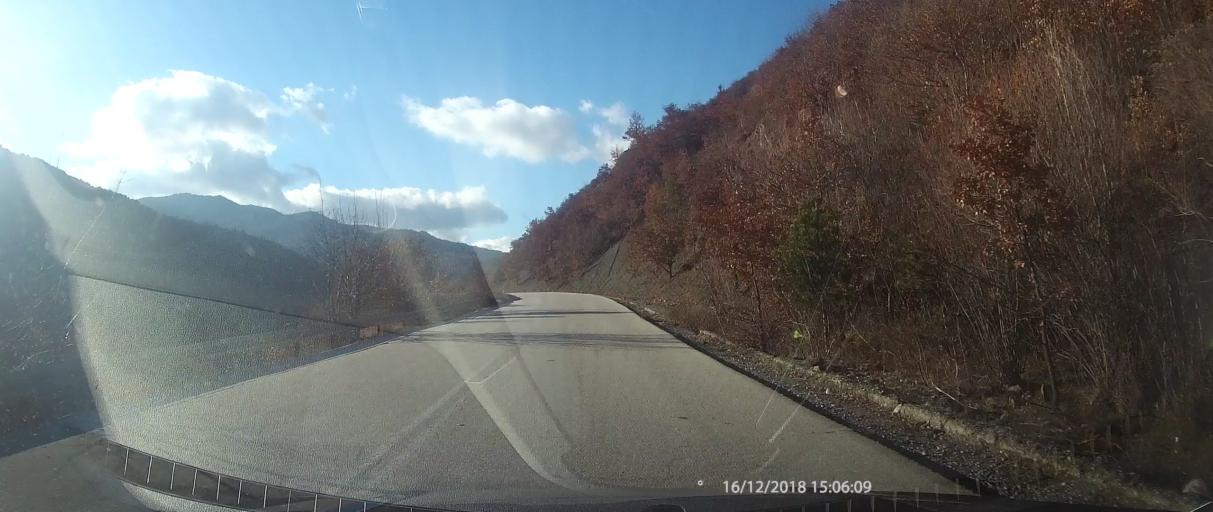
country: GR
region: West Macedonia
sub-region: Nomos Kastorias
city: Nestorio
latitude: 40.2205
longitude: 20.9477
